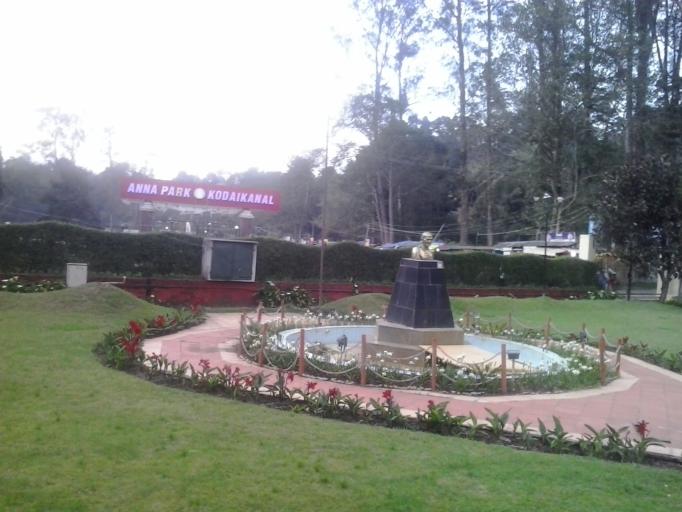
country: IN
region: Tamil Nadu
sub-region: Dindigul
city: Kodaikanal
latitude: 10.2309
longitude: 77.4919
